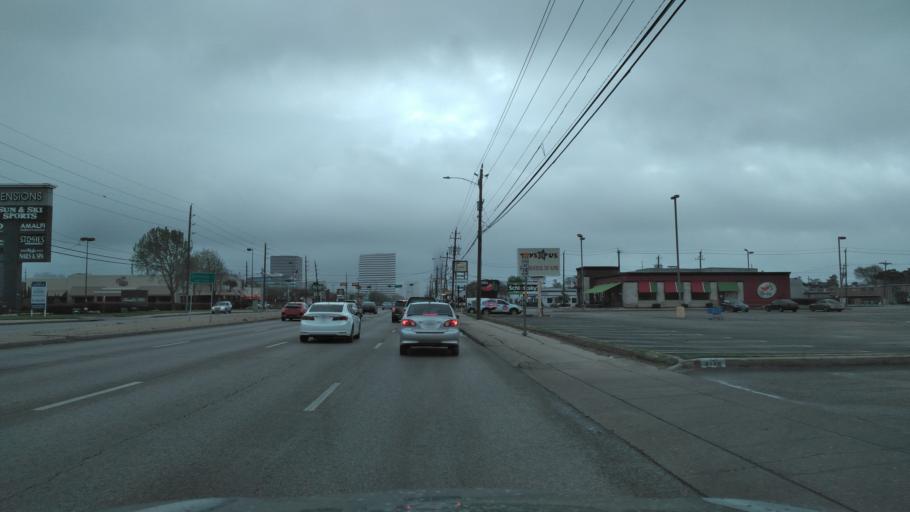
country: US
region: Texas
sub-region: Harris County
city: Hunters Creek Village
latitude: 29.7381
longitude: -95.4910
